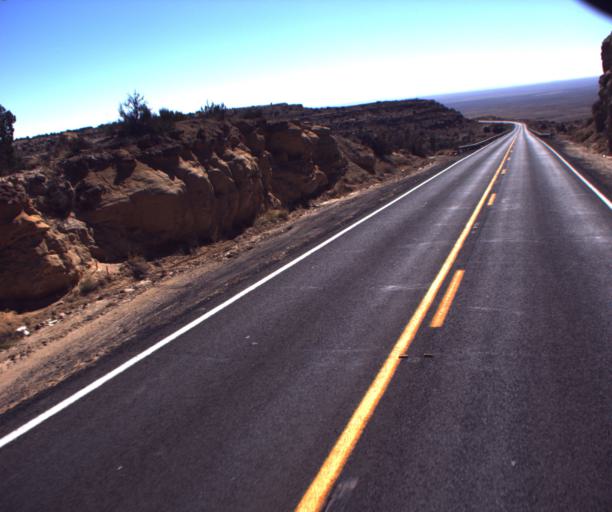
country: US
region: Arizona
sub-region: Navajo County
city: First Mesa
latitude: 35.9010
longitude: -110.6653
